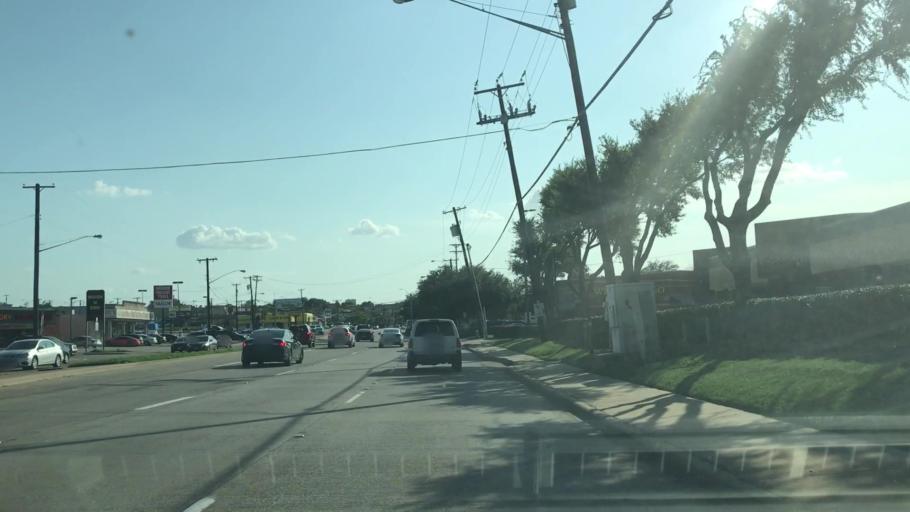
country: US
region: Texas
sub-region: Dallas County
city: Highland Park
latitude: 32.8664
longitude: -96.7418
